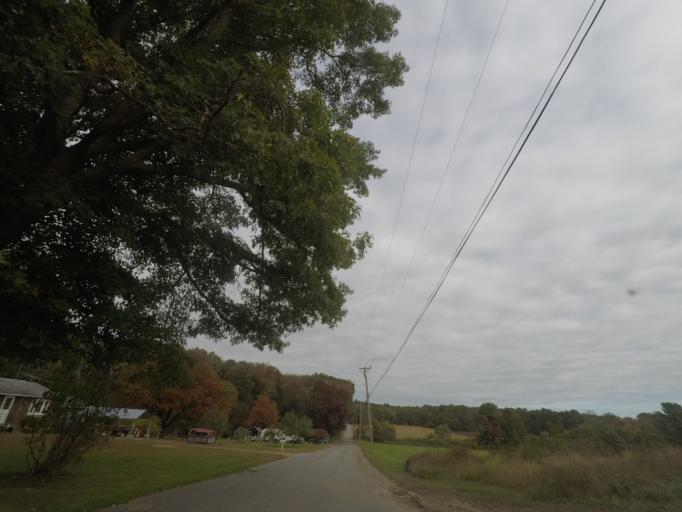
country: US
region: Connecticut
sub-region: Windham County
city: Thompson
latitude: 41.9577
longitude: -71.8337
